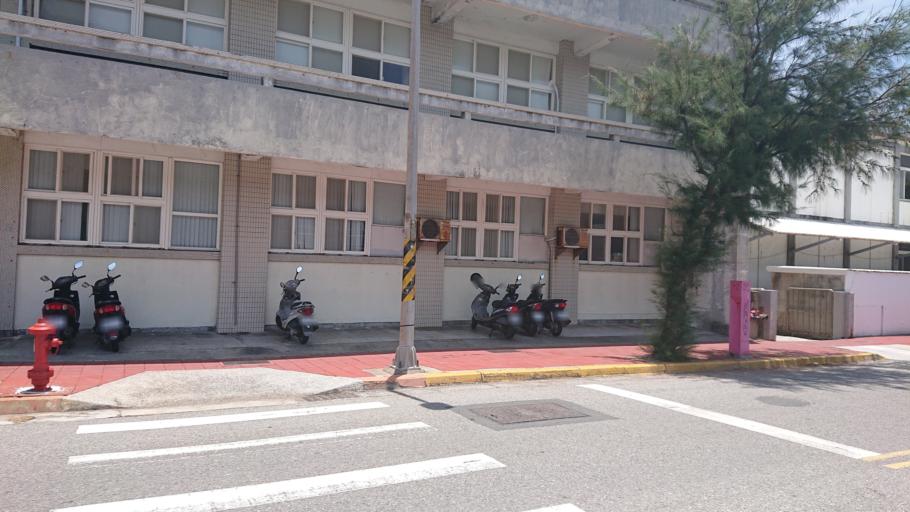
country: TW
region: Taiwan
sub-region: Penghu
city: Ma-kung
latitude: 23.5697
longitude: 119.5662
